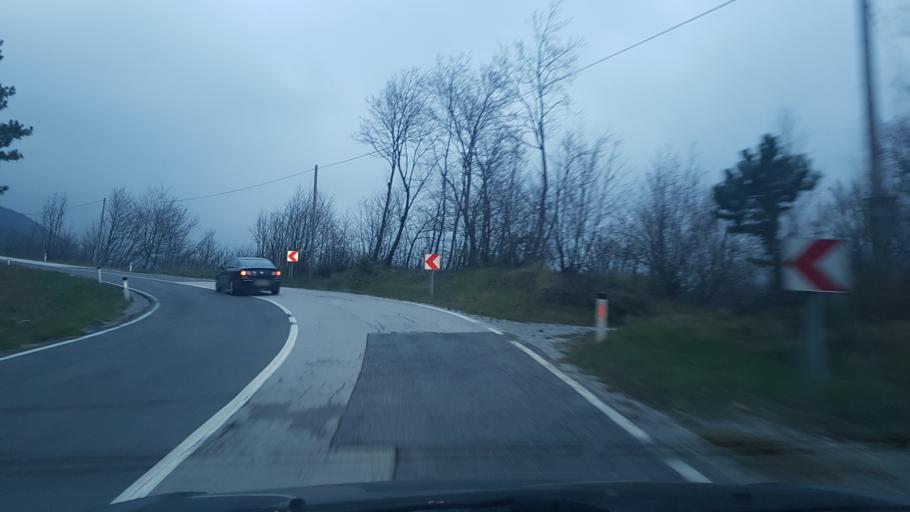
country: SI
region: Vipava
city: Vipava
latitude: 45.8819
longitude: 13.9791
